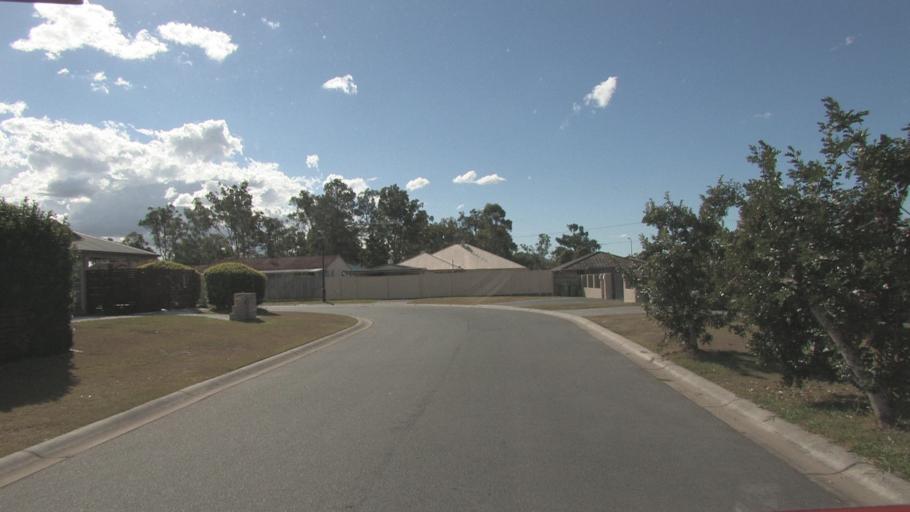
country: AU
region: Queensland
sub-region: Logan
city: Logan Reserve
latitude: -27.6956
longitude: 153.0946
